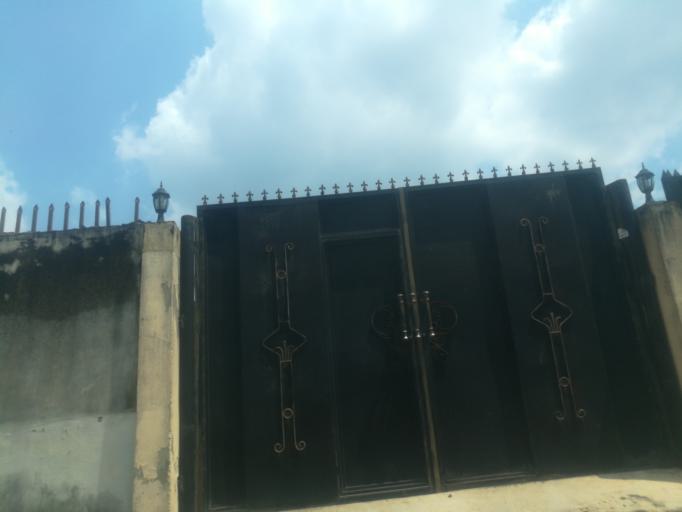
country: NG
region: Oyo
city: Ibadan
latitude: 7.3936
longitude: 3.9650
